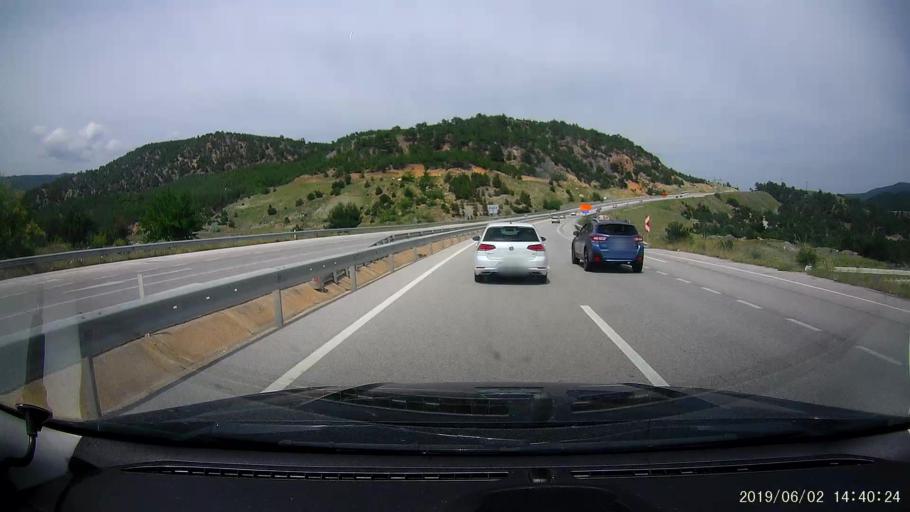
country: TR
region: Corum
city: Hacihamza
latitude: 41.0821
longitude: 34.3177
